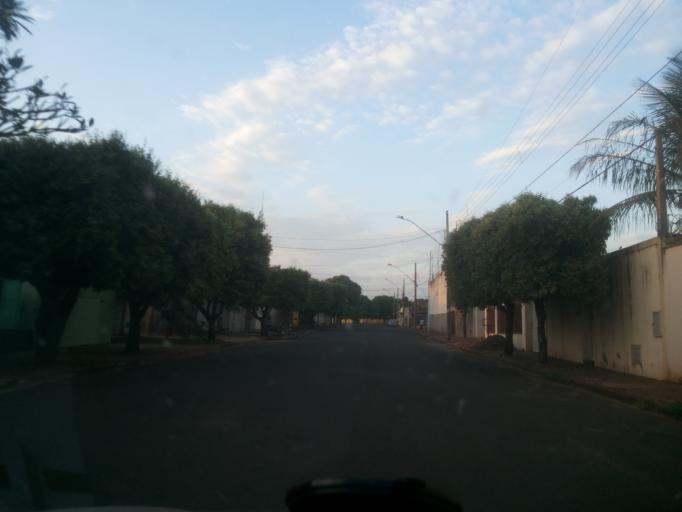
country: BR
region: Minas Gerais
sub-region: Ituiutaba
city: Ituiutaba
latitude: -18.9820
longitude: -49.4548
